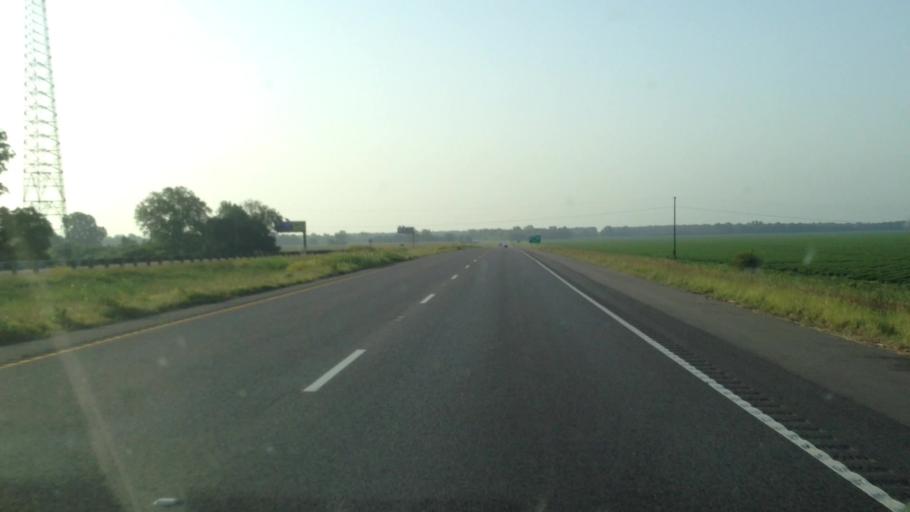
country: US
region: Louisiana
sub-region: Rapides Parish
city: Boyce
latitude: 31.3921
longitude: -92.6925
